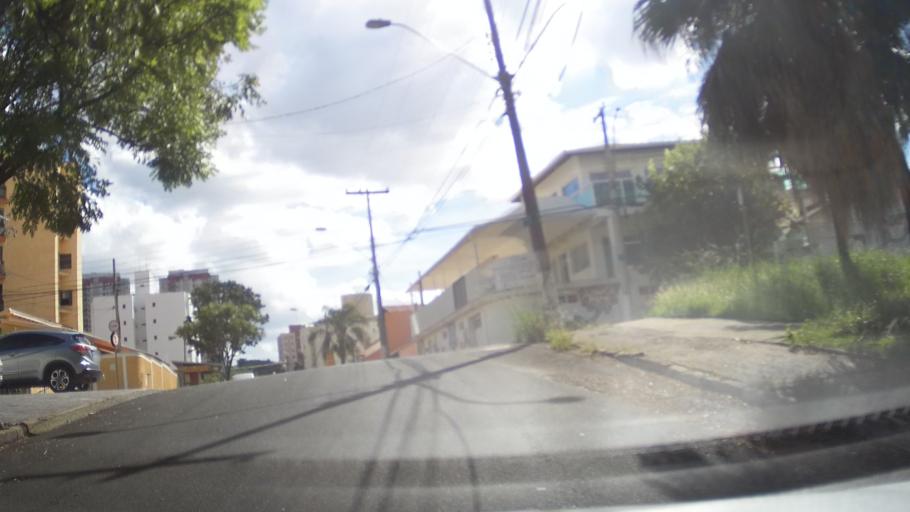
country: BR
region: Sao Paulo
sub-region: Campinas
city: Campinas
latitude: -22.9190
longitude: -47.0469
